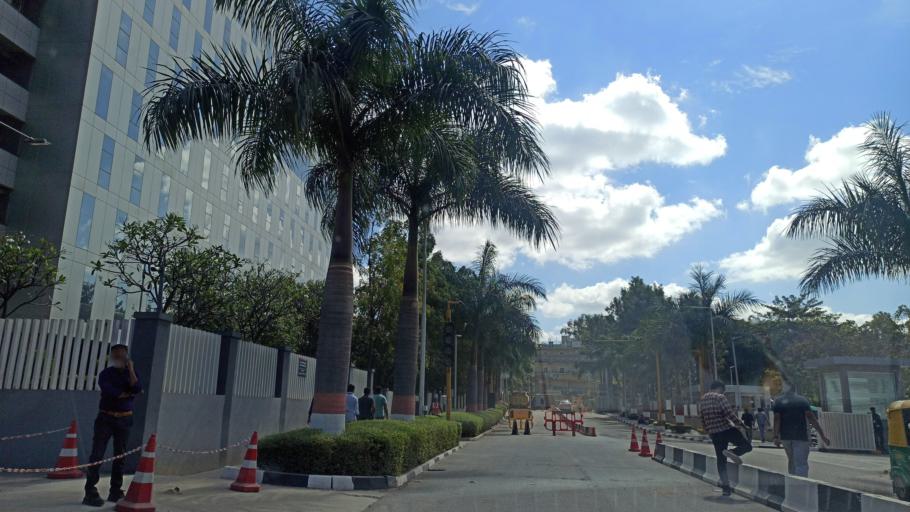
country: IN
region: Karnataka
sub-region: Bangalore Urban
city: Bangalore
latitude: 12.9199
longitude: 77.6855
